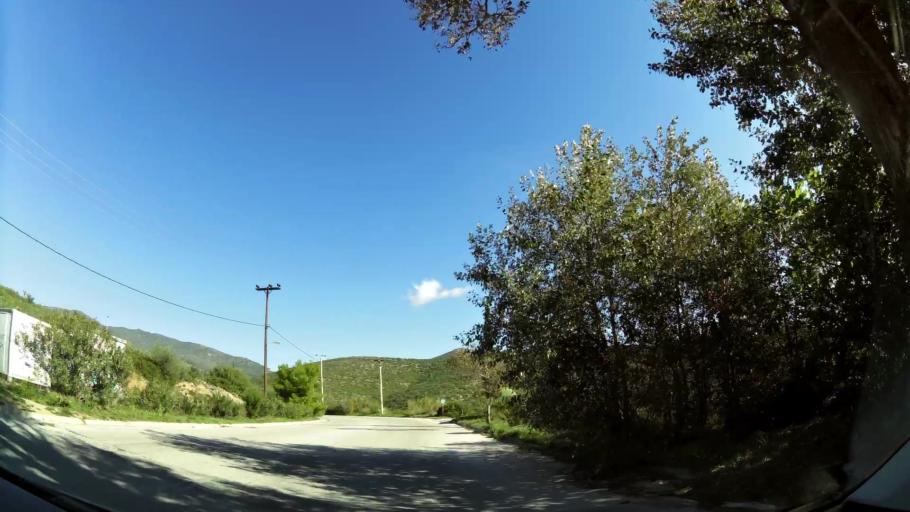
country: GR
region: Attica
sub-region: Nomarchia Anatolikis Attikis
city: Dhrafi
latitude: 38.0295
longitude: 23.9063
